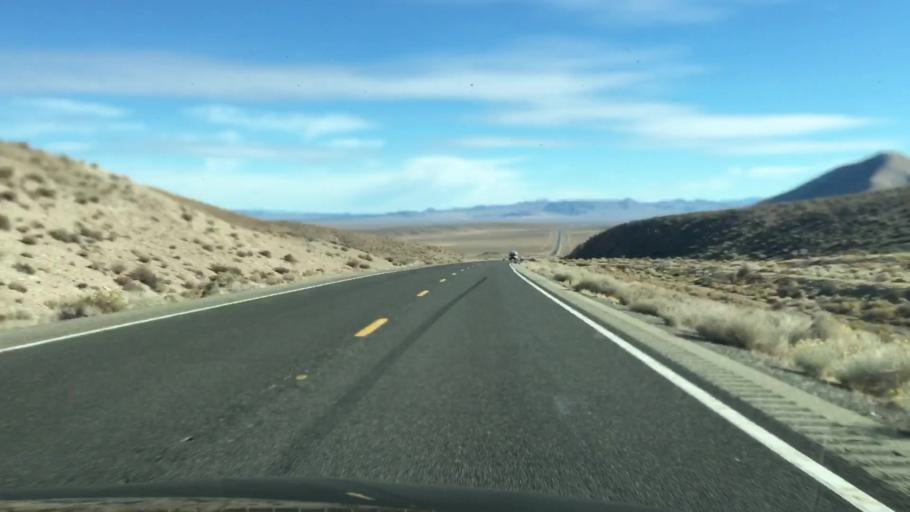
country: US
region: Nevada
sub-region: Lyon County
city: Yerington
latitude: 39.0366
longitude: -118.9294
